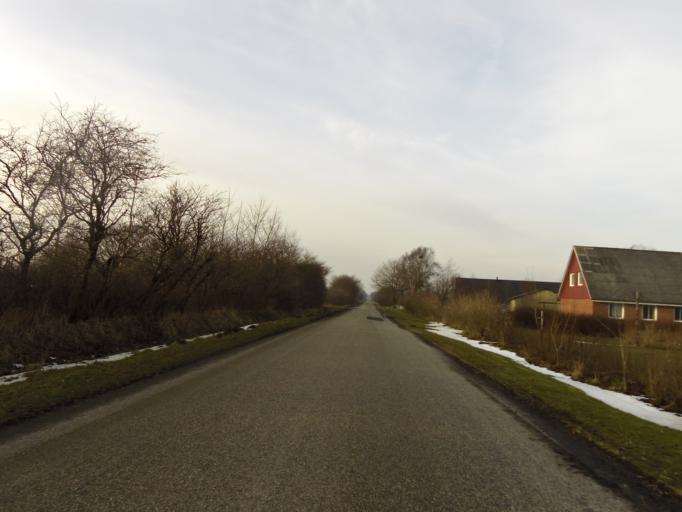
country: DK
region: South Denmark
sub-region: Tonder Kommune
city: Logumkloster
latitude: 55.1659
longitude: 8.8974
